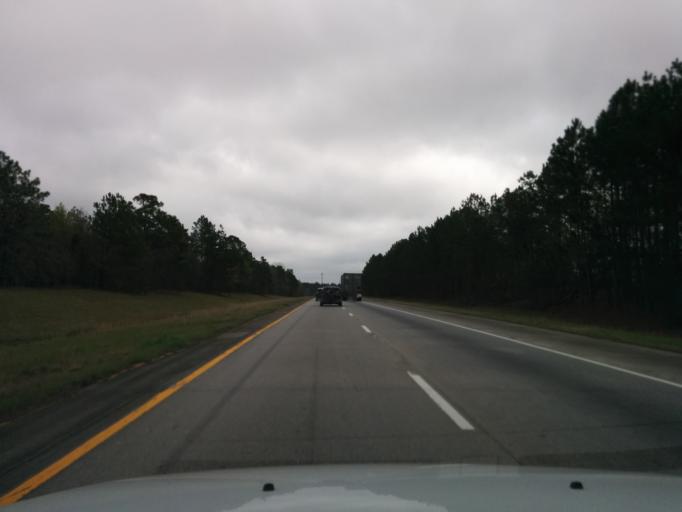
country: US
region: Georgia
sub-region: Candler County
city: Metter
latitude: 32.3823
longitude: -82.2323
